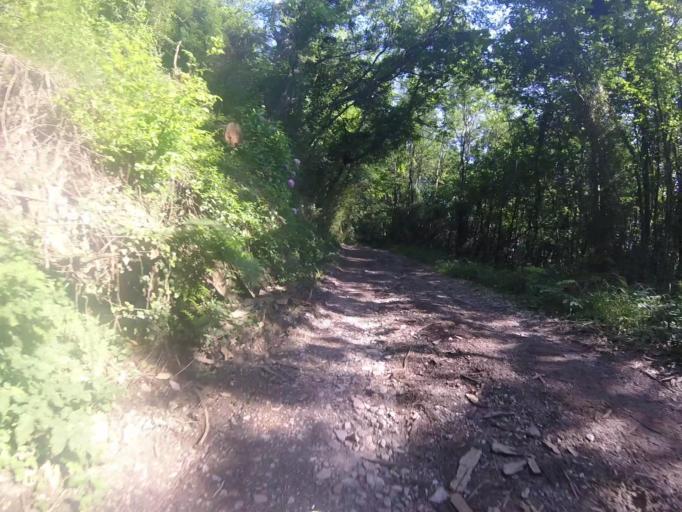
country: ES
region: Basque Country
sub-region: Provincia de Guipuzcoa
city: Astigarraga
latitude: 43.2627
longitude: -1.9361
